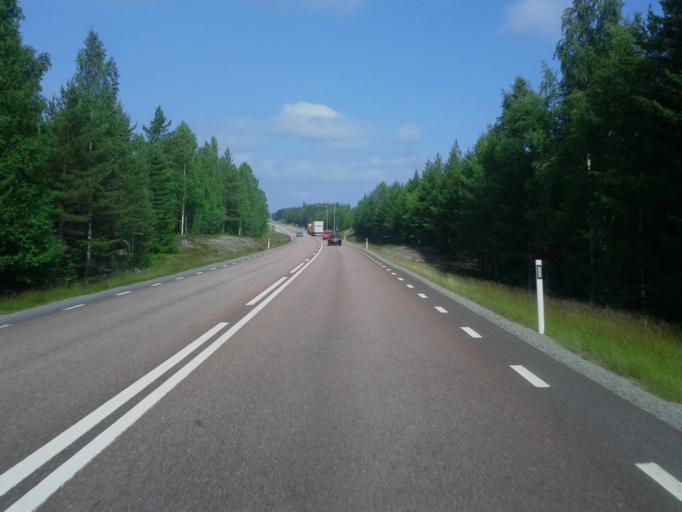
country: SE
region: Vaesterbotten
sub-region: Skelleftea Kommun
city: Burea
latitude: 64.6286
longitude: 21.1776
